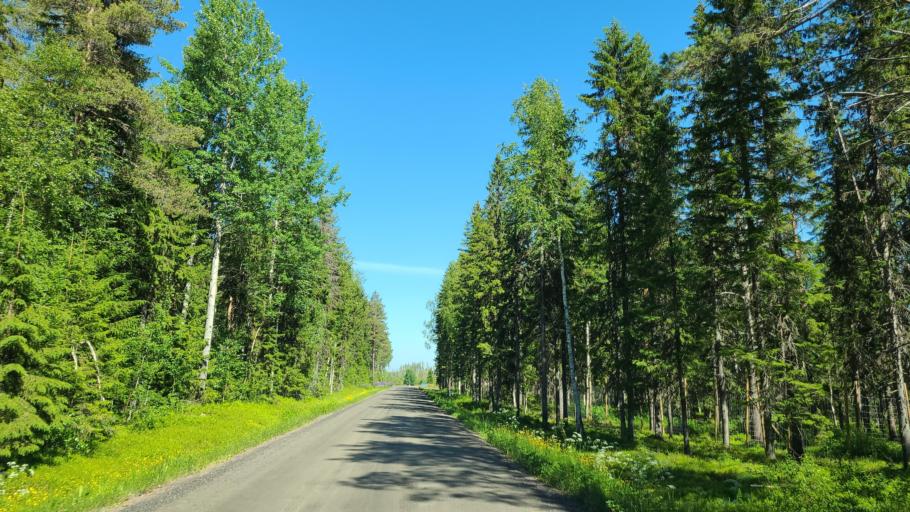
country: SE
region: Vaesterbotten
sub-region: Bjurholms Kommun
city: Bjurholm
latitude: 63.6412
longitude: 19.1113
